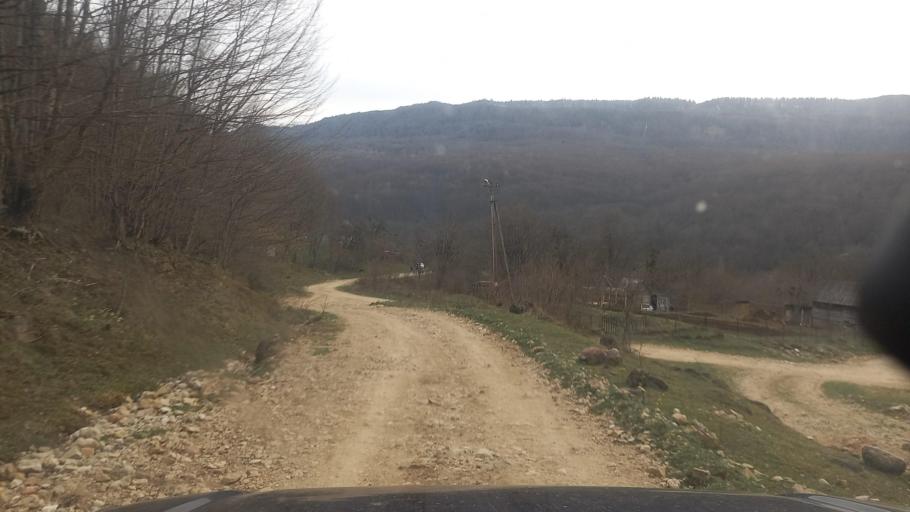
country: RU
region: Adygeya
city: Kamennomostskiy
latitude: 44.1955
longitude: 39.9656
